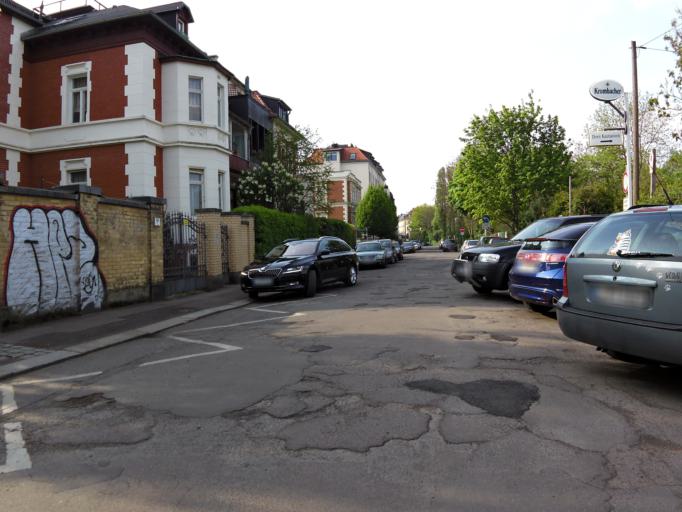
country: DE
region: Saxony
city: Leipzig
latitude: 51.3177
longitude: 12.3459
